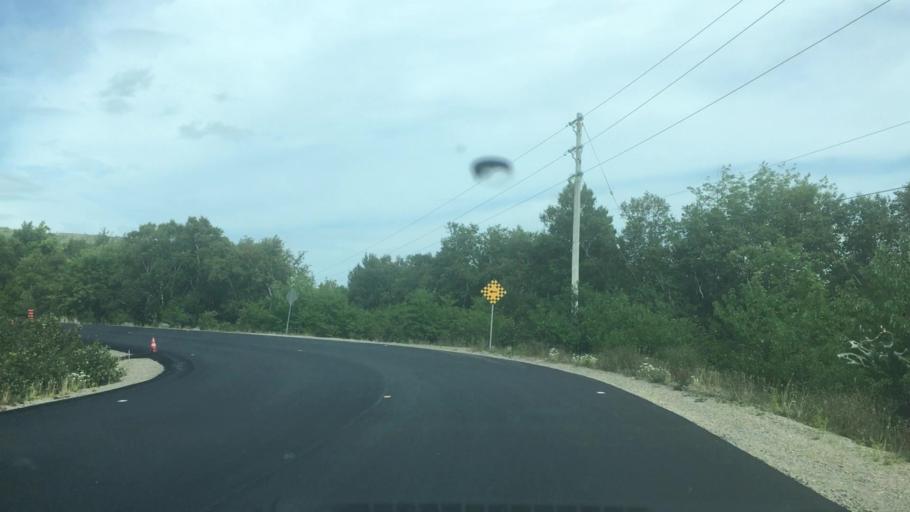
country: CA
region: Nova Scotia
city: Sydney Mines
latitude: 46.5701
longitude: -60.3938
